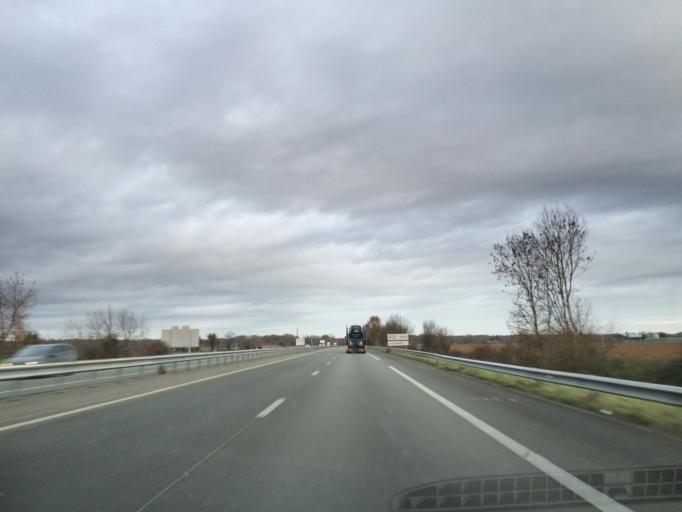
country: FR
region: Poitou-Charentes
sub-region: Departement des Deux-Sevres
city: Pamproux
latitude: 46.4219
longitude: -0.0983
